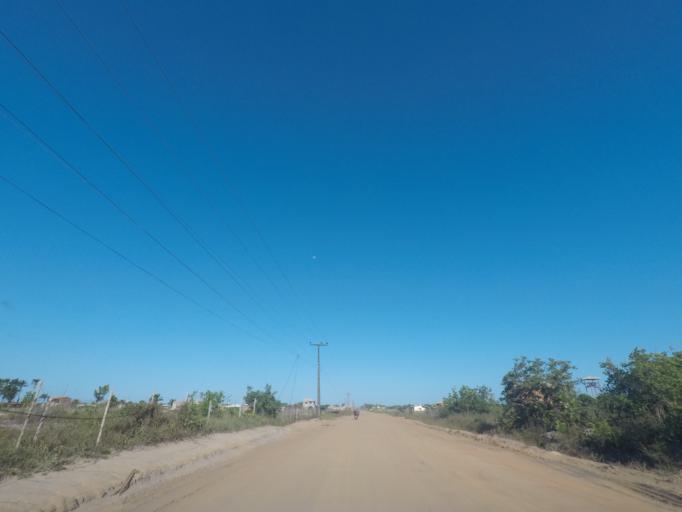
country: BR
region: Bahia
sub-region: Camamu
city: Camamu
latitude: -13.9328
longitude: -38.9457
